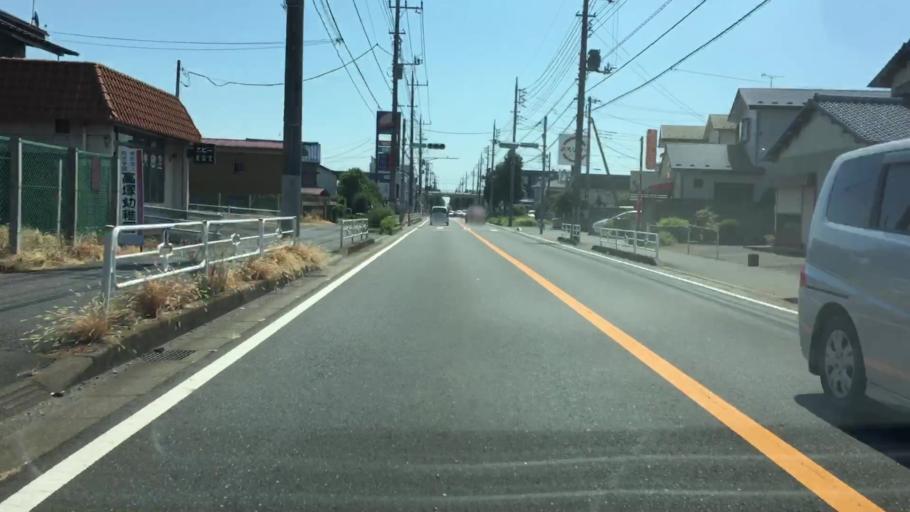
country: JP
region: Chiba
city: Matsudo
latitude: 35.7585
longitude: 139.9366
